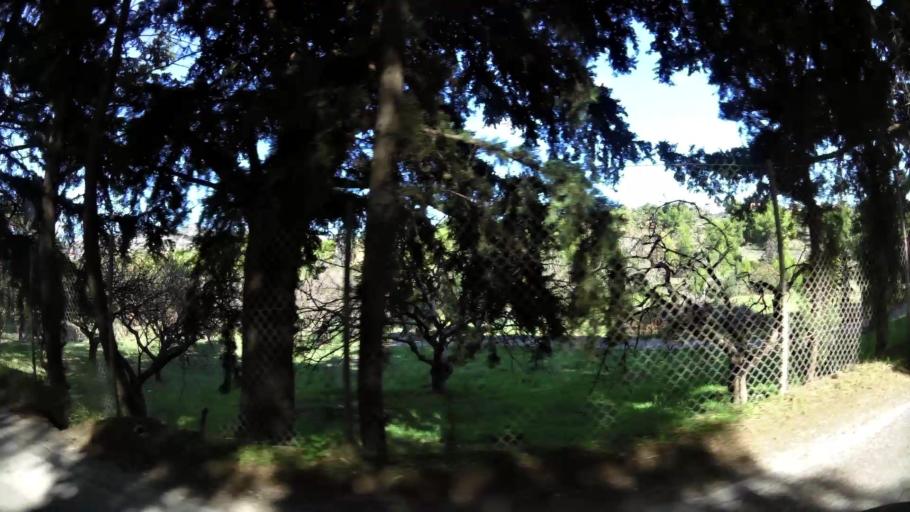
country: GR
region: Attica
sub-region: Nomarchia Anatolikis Attikis
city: Dioni
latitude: 38.0151
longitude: 23.9310
